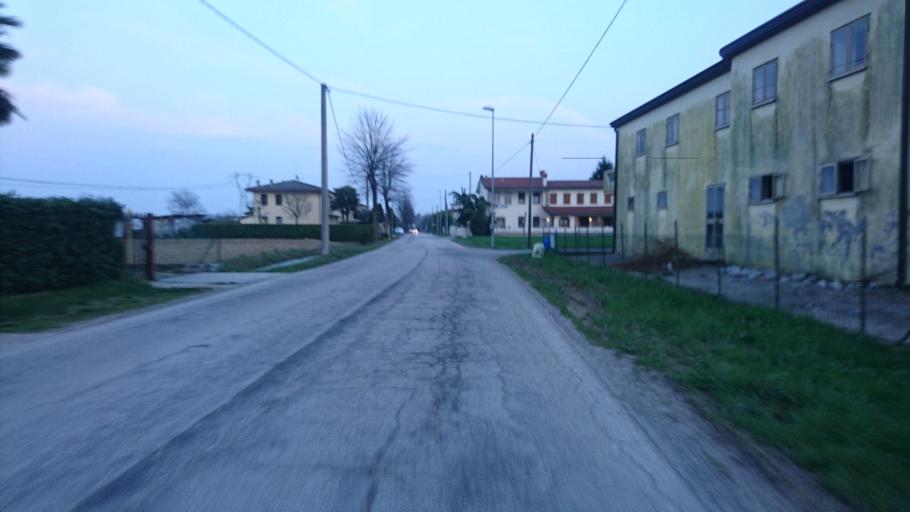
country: IT
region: Veneto
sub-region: Provincia di Padova
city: Saccolongo
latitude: 45.3928
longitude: 11.7469
